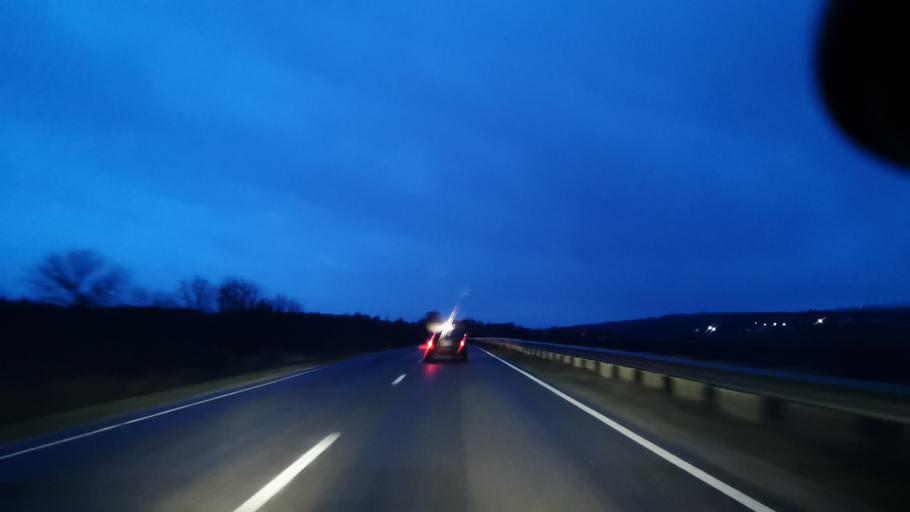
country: MD
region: Orhei
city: Orhei
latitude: 47.4092
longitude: 28.8149
